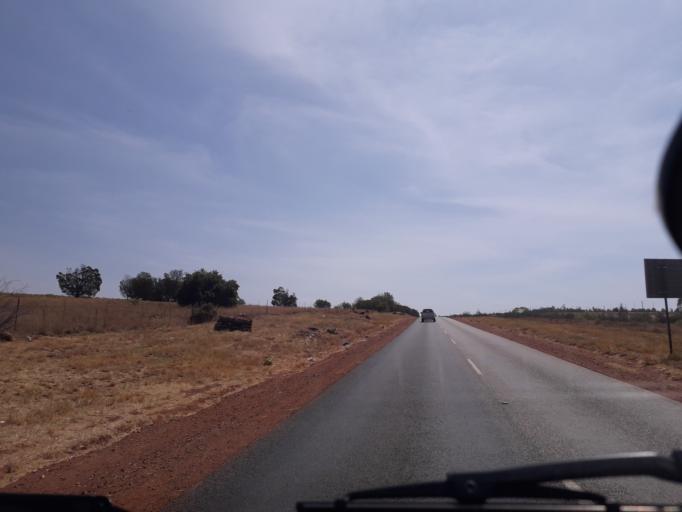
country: ZA
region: Gauteng
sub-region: West Rand District Municipality
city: Krugersdorp
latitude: -25.9955
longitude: 27.6994
